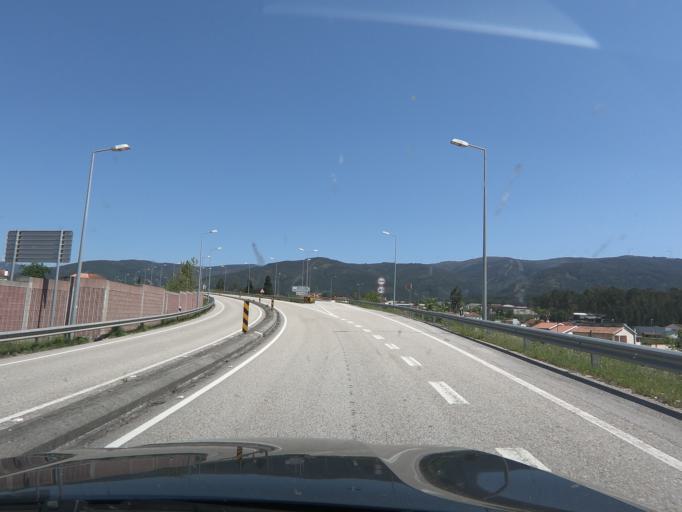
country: PT
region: Coimbra
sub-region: Miranda do Corvo
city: Miranda do Corvo
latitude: 40.0838
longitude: -8.3301
